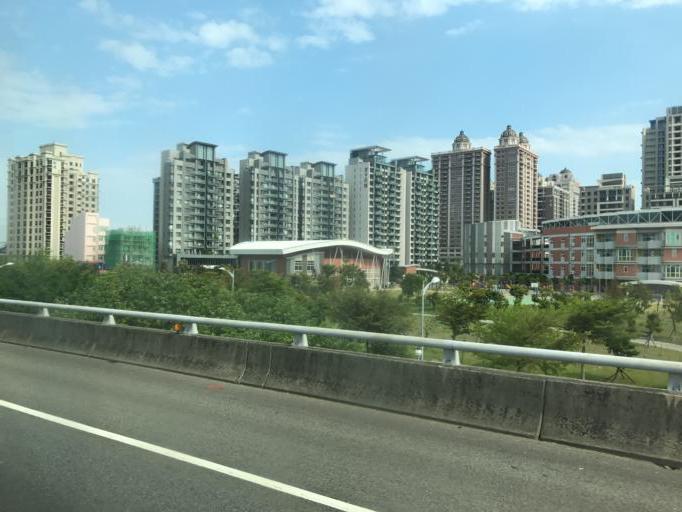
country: TW
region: Taiwan
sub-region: Hsinchu
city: Zhubei
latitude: 24.8165
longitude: 121.0131
